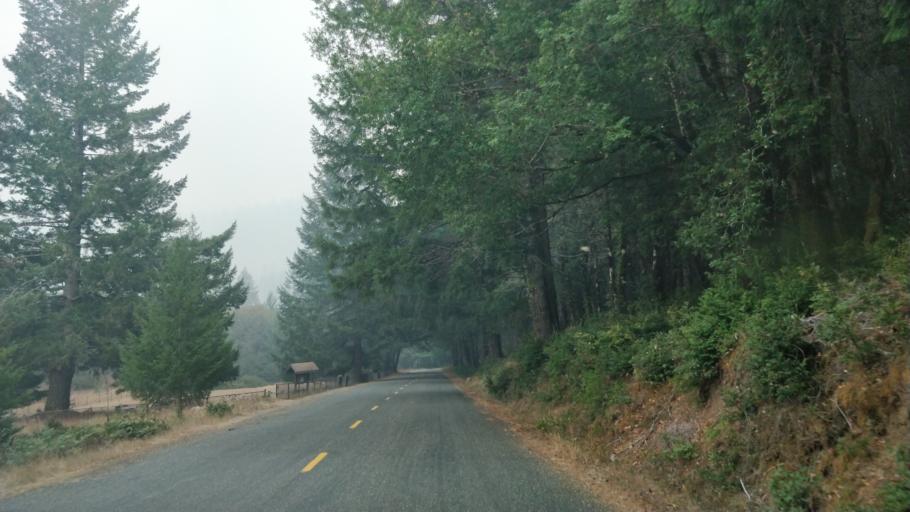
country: US
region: California
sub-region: Humboldt County
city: Rio Dell
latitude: 40.3320
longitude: -124.0342
